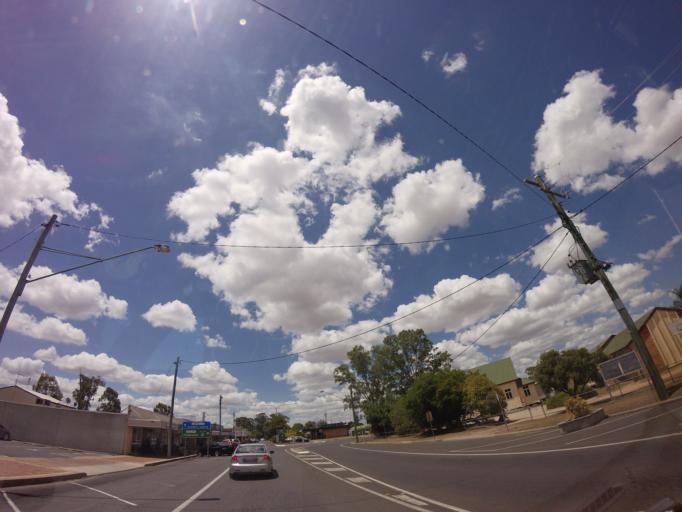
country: AU
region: Queensland
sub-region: Toowoomba
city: Oakey
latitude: -27.8773
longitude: 151.2697
